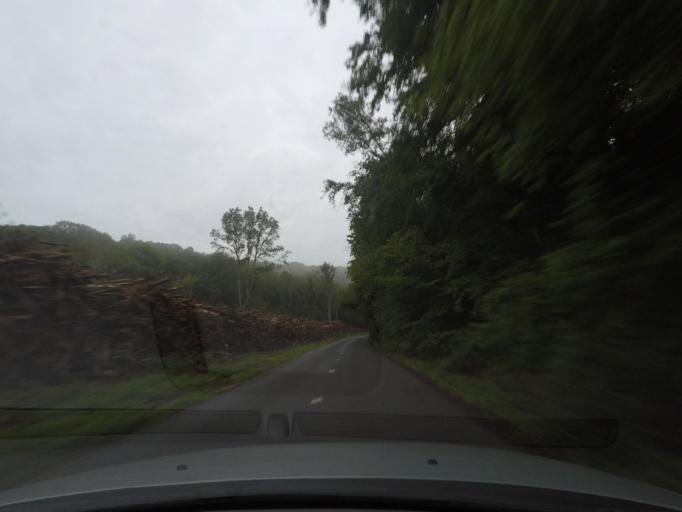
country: FR
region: Haute-Normandie
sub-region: Departement de la Seine-Maritime
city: Fontaine-le-Bourg
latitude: 49.5509
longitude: 1.1219
